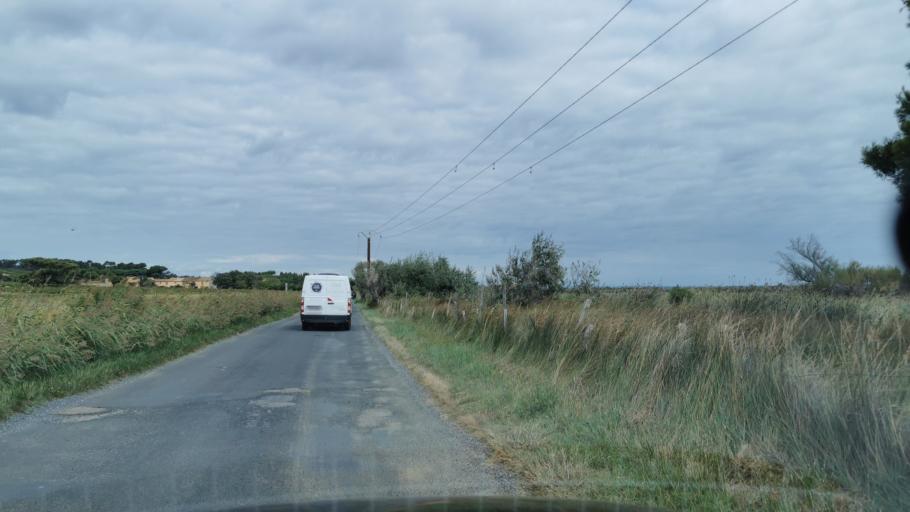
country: FR
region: Languedoc-Roussillon
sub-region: Departement de l'Aude
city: Fleury
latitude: 43.1987
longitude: 3.1912
